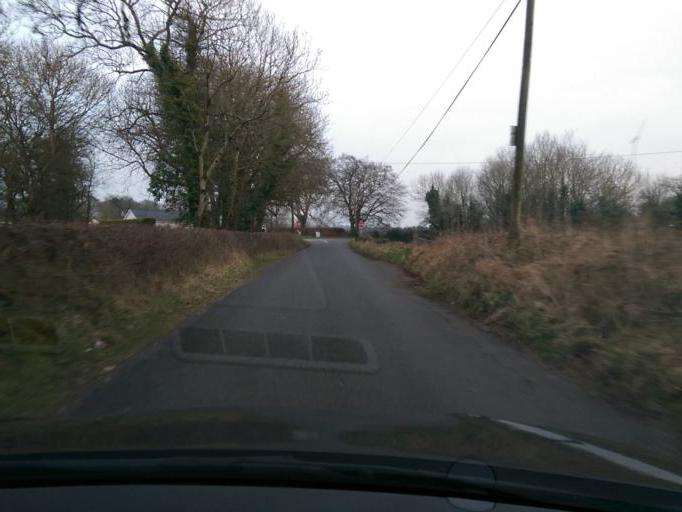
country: IE
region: Leinster
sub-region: An Longfort
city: Ballymahon
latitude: 53.5411
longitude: -7.7906
